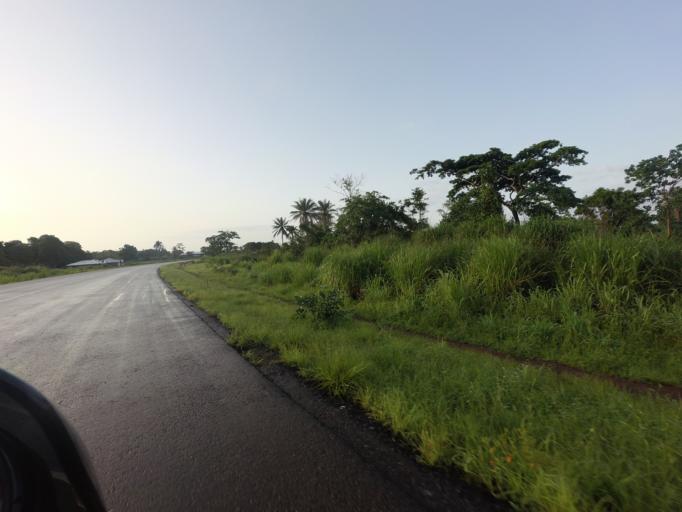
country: SL
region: Northern Province
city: Kambia
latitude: 9.0965
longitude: -12.9121
